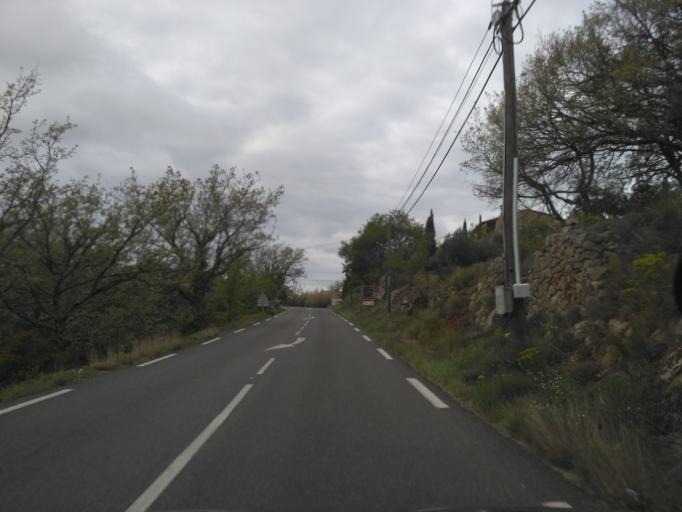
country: FR
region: Provence-Alpes-Cote d'Azur
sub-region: Departement du Var
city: Saint-Julien
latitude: 43.6328
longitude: 5.9388
